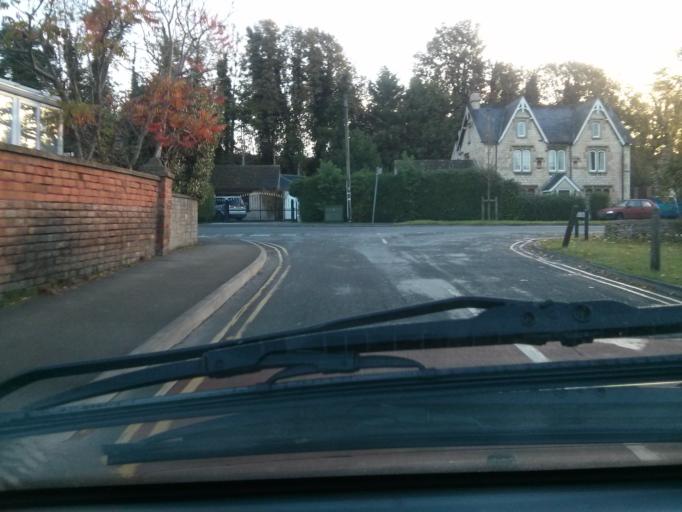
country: GB
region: England
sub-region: Gloucestershire
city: Stonehouse
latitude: 51.7485
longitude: -2.2840
